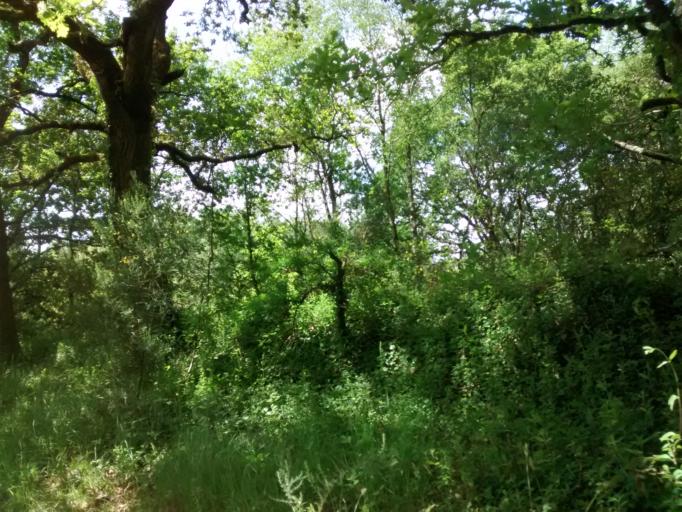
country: FR
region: Brittany
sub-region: Departement du Morbihan
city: Larmor-Baden
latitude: 47.6006
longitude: -2.9023
